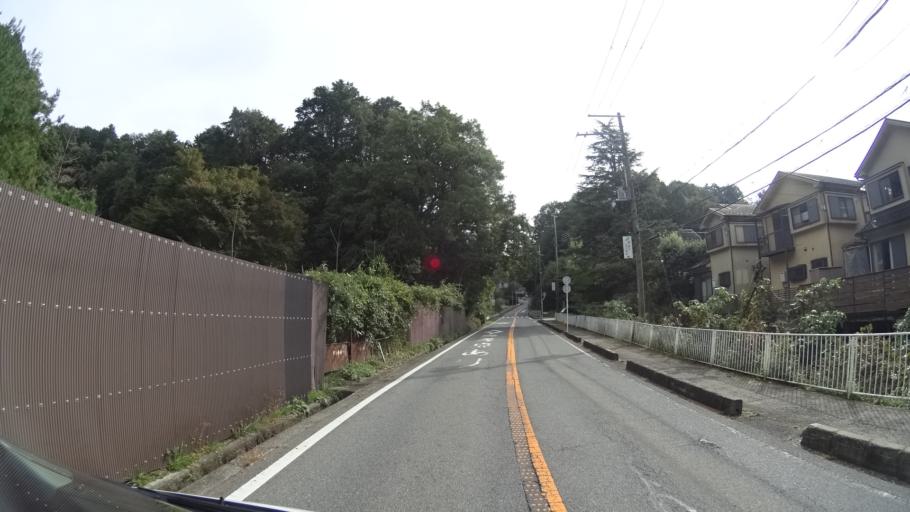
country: JP
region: Shiga Prefecture
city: Otsu-shi
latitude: 35.0340
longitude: 135.8322
